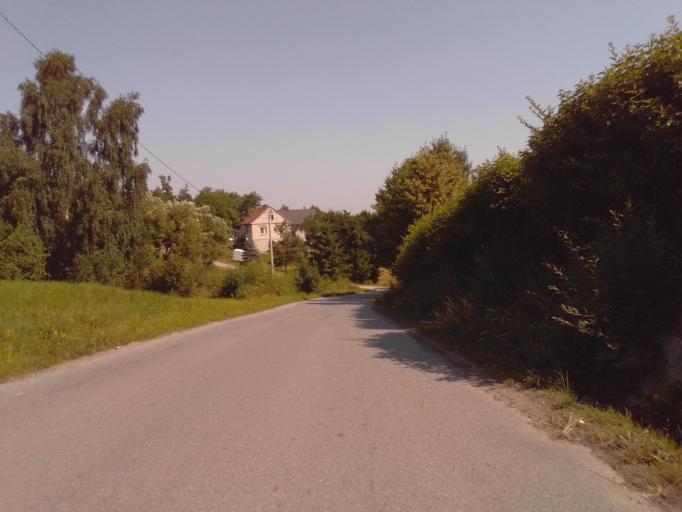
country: PL
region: Subcarpathian Voivodeship
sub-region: Powiat ropczycko-sedziszowski
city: Zagorzyce
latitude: 50.0111
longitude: 21.6347
